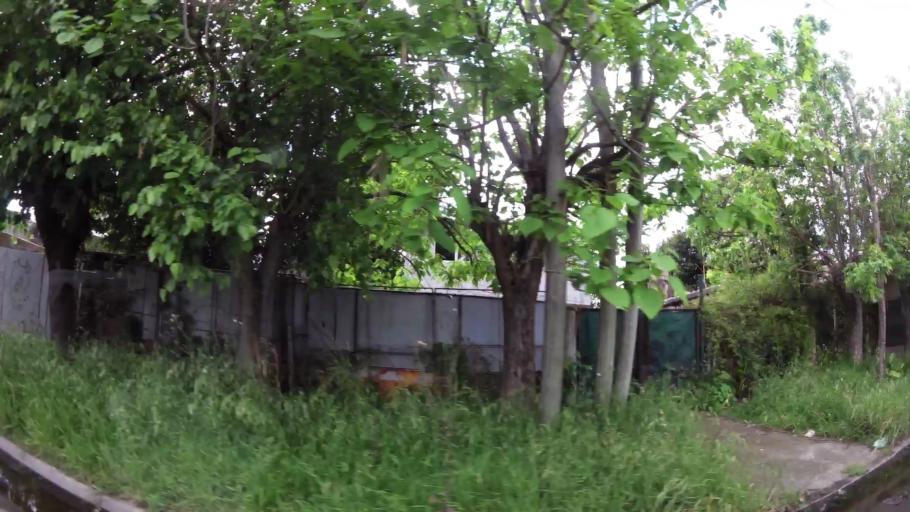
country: AR
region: Buenos Aires
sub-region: Partido de Quilmes
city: Quilmes
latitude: -34.8365
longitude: -58.1847
